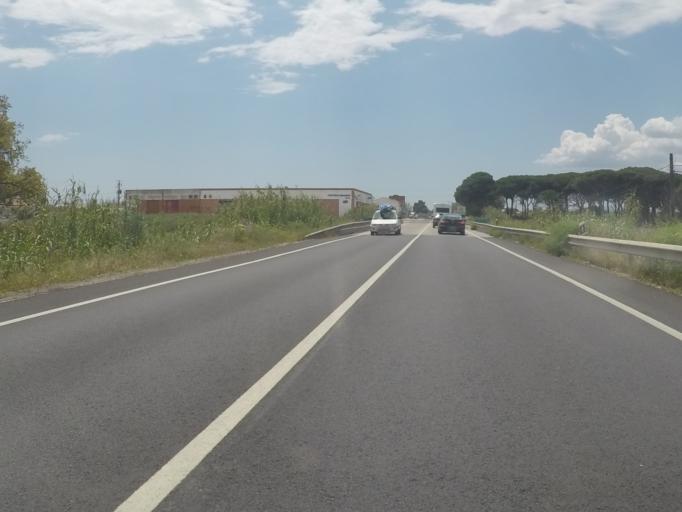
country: PT
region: Setubal
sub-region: Setubal
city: Setubal
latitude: 38.5541
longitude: -8.8053
